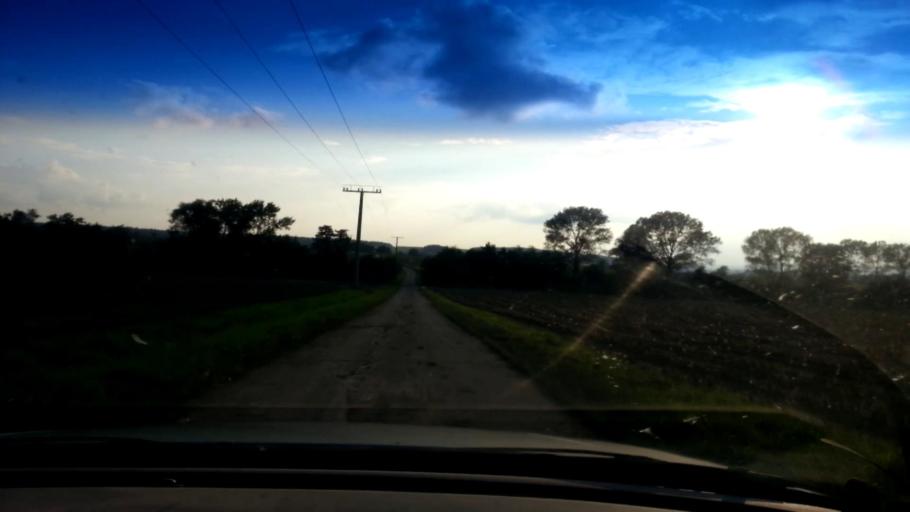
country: DE
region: Bavaria
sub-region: Upper Franconia
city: Litzendorf
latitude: 49.9496
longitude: 11.0086
